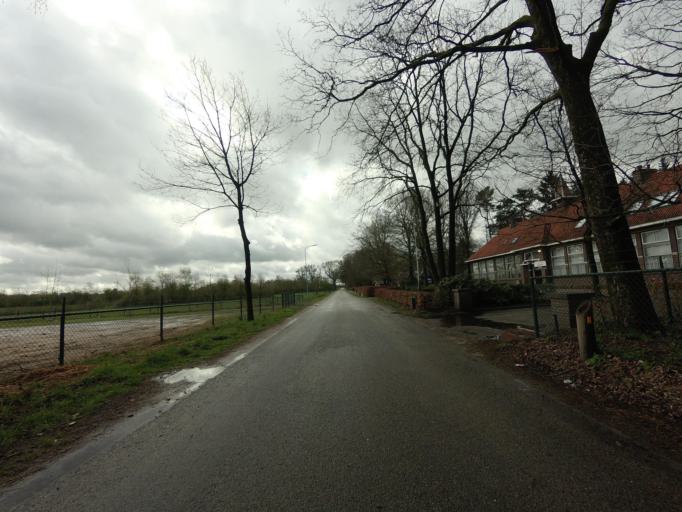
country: NL
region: Gelderland
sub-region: Gemeente Barneveld
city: Stroe
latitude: 52.1844
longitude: 5.6792
